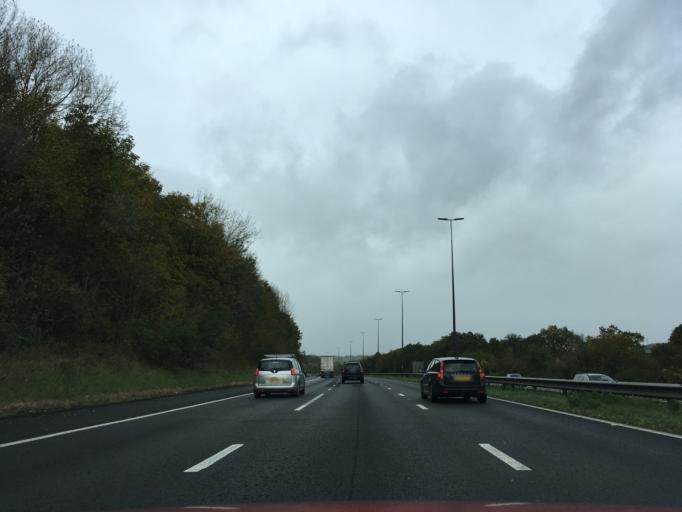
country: GB
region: Wales
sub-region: Newport
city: Bishton
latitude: 51.5993
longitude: -2.8834
